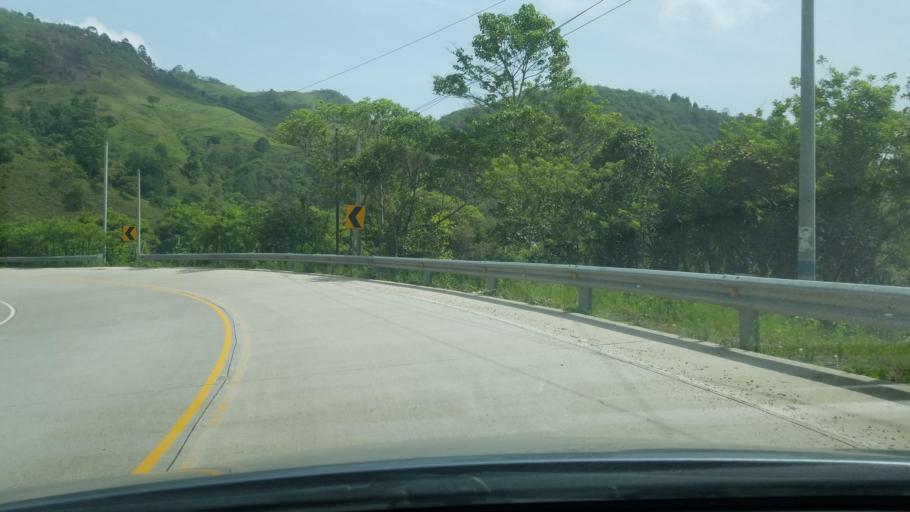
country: HN
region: Copan
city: San Jeronimo
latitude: 14.9541
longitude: -88.9069
